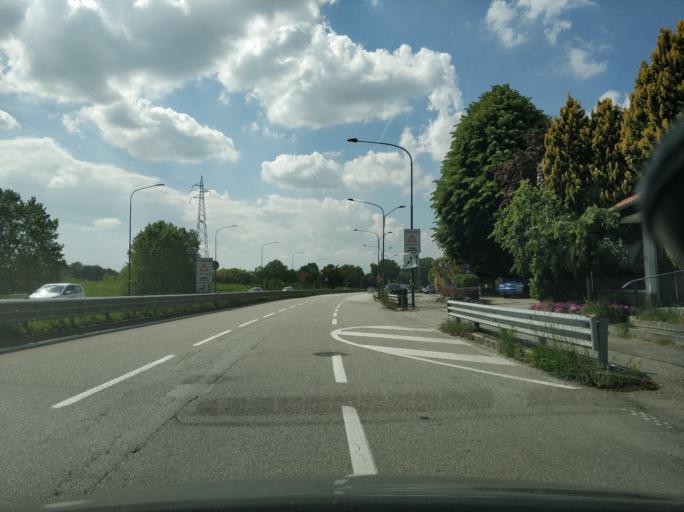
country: IT
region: Piedmont
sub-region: Provincia di Torino
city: San Mauro Torinese
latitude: 45.0953
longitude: 7.7293
